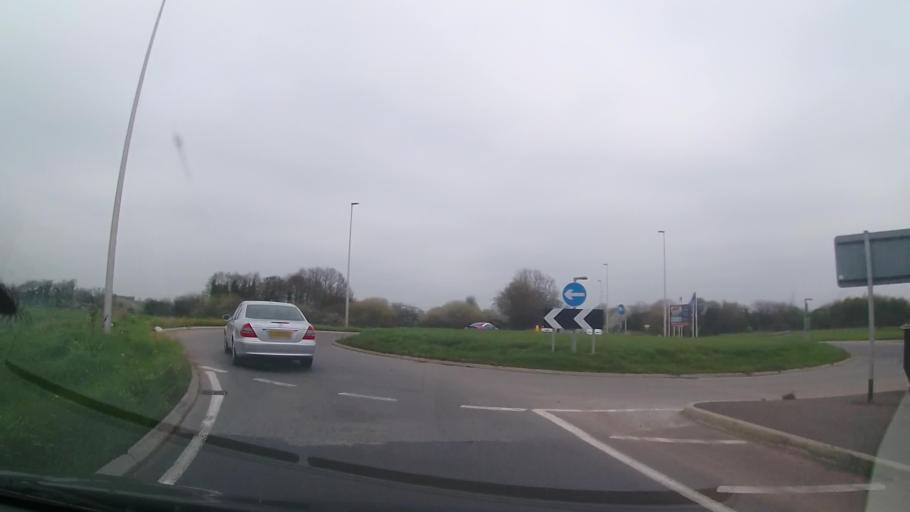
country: GB
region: England
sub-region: Shropshire
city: Market Drayton
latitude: 52.9101
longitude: -2.5021
